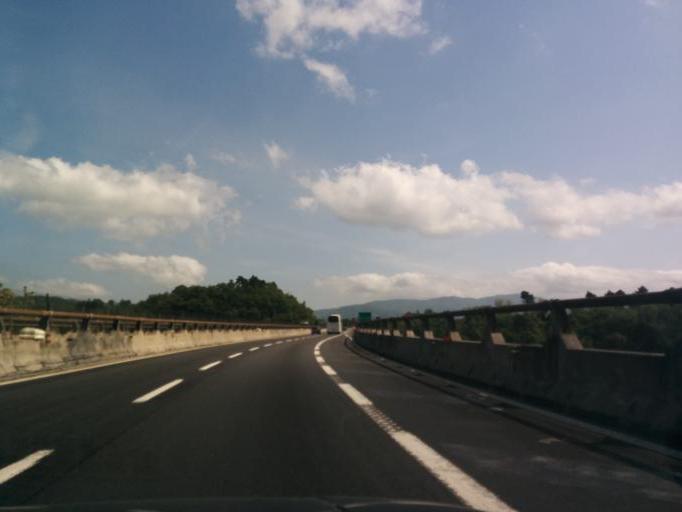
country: IT
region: Tuscany
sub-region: Province of Florence
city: Barberino di Mugello
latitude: 44.0261
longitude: 11.2224
